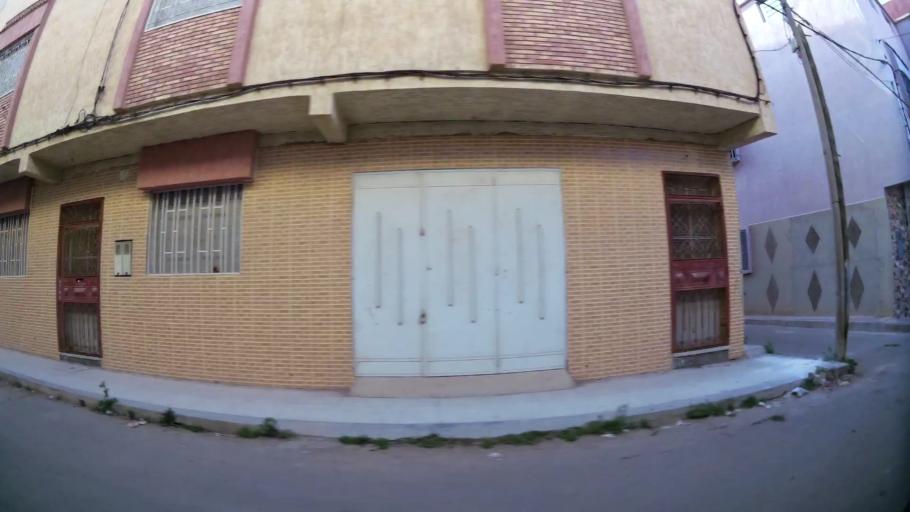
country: MA
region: Oriental
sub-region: Oujda-Angad
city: Oujda
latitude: 34.6761
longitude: -1.8925
